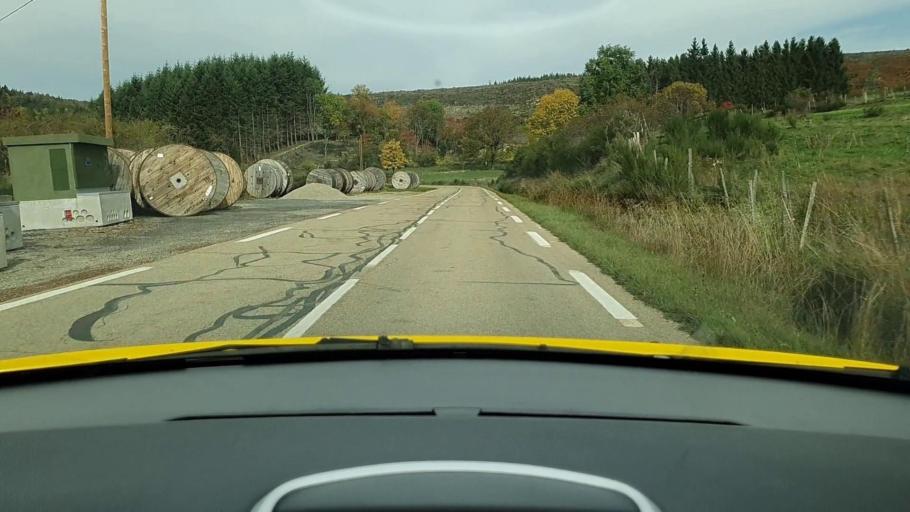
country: FR
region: Languedoc-Roussillon
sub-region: Departement de la Lozere
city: Meyrueis
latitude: 44.1198
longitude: 3.4848
